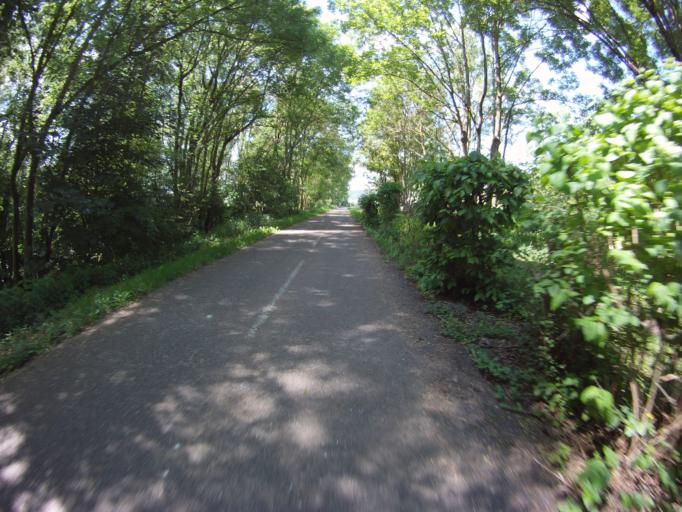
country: FR
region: Lorraine
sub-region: Departement de Meurthe-et-Moselle
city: Eulmont
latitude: 48.7437
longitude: 6.2143
